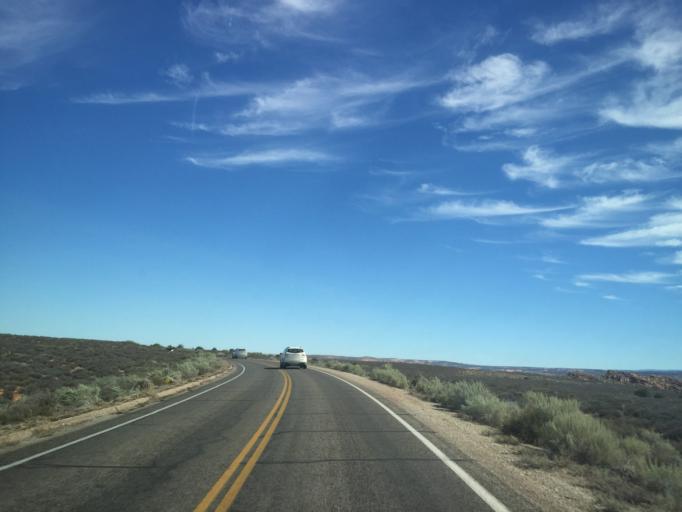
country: US
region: Utah
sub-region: Grand County
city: Moab
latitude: 38.7140
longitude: -109.5573
